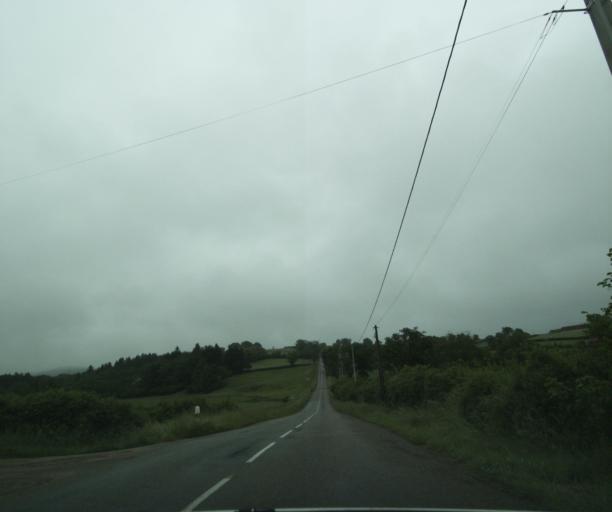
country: FR
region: Bourgogne
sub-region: Departement de Saone-et-Loire
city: Charolles
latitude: 46.4352
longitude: 4.4128
